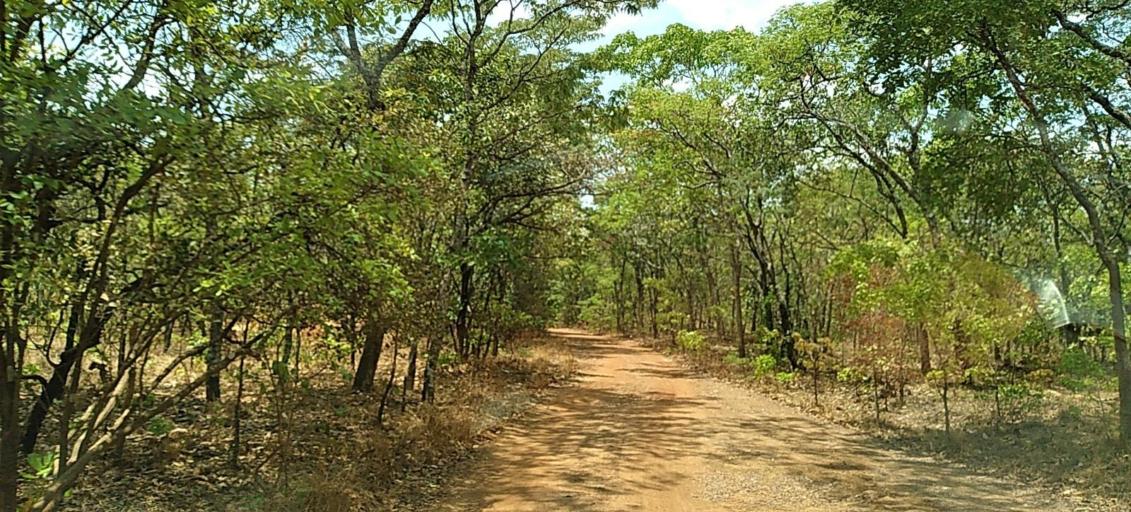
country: ZM
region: Copperbelt
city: Chililabombwe
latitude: -12.5007
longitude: 27.6391
